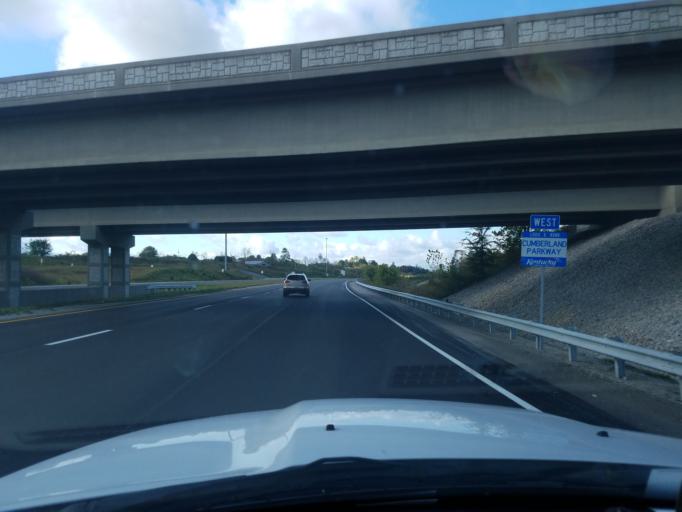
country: US
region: Kentucky
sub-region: Pulaski County
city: Somerset
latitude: 37.1050
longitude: -84.6626
